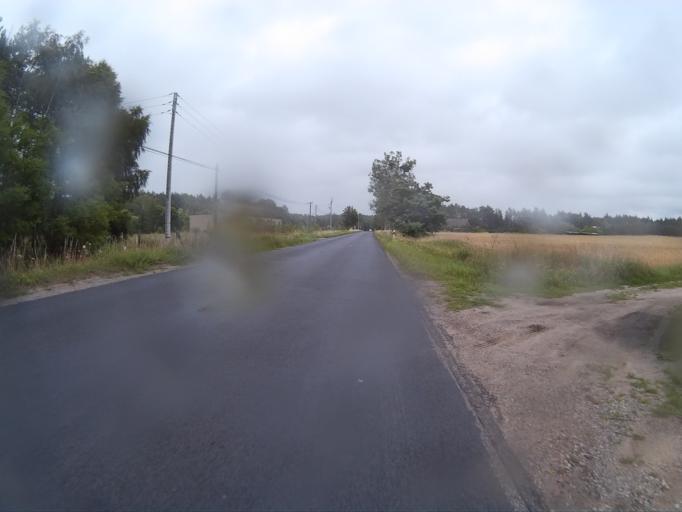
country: PL
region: Kujawsko-Pomorskie
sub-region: Powiat tucholski
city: Tuchola
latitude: 53.6013
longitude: 17.9138
